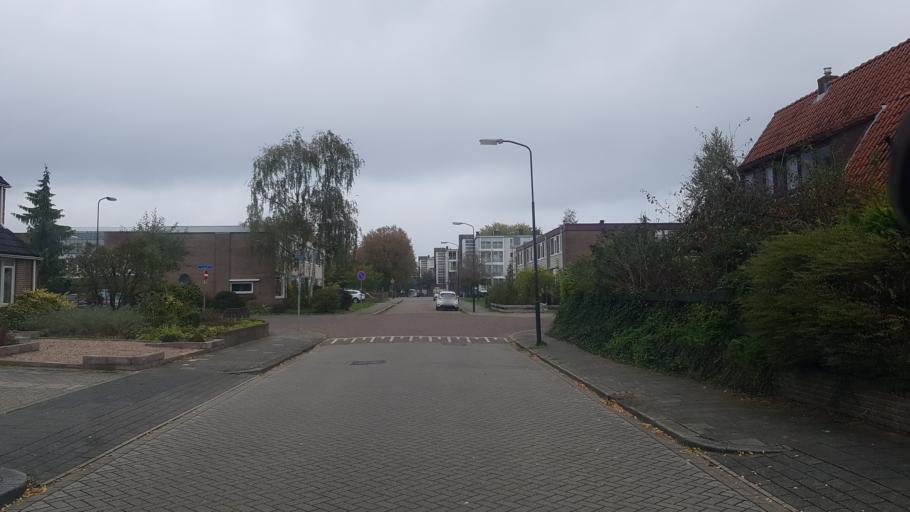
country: NL
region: Gelderland
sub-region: Gemeente Apeldoorn
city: Apeldoorn
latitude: 52.2029
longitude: 5.9381
